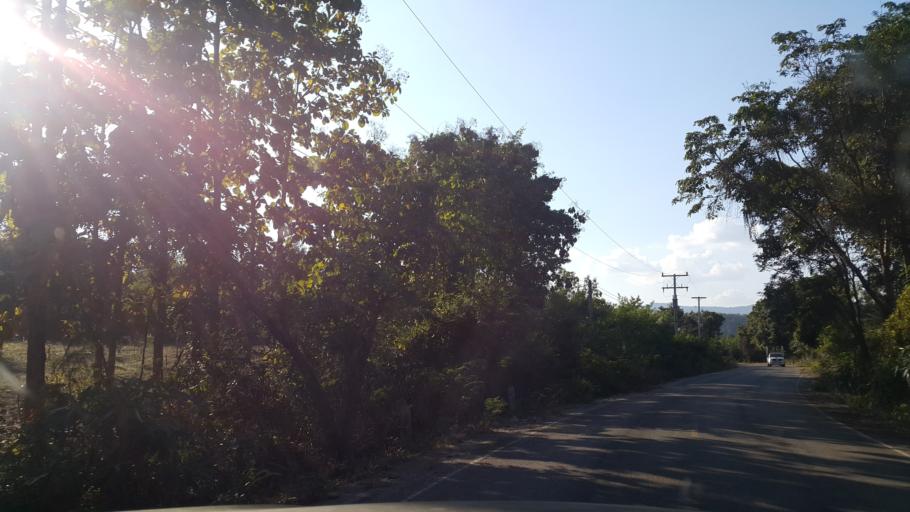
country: TH
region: Sukhothai
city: Thung Saliam
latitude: 17.3881
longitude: 99.5168
